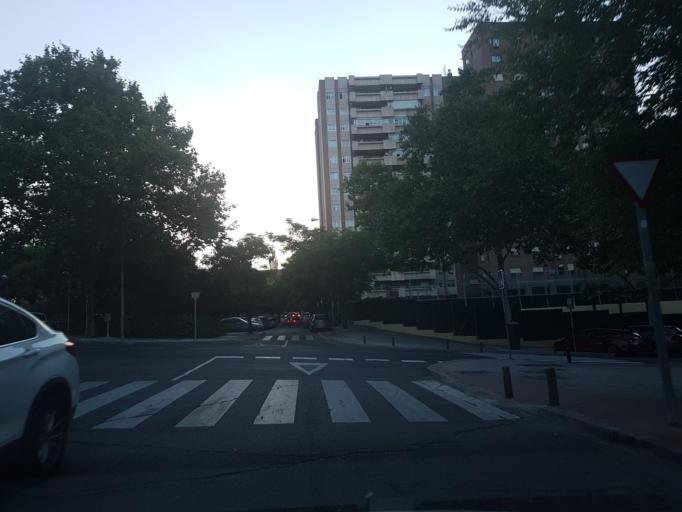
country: ES
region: Madrid
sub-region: Provincia de Madrid
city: Pinar de Chamartin
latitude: 40.4754
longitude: -3.6653
